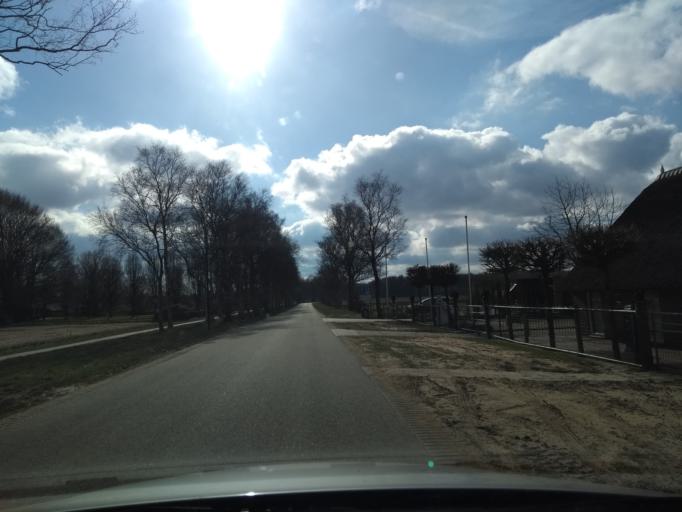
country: NL
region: Drenthe
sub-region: Gemeente Westerveld
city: Dwingeloo
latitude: 52.8272
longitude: 6.3696
